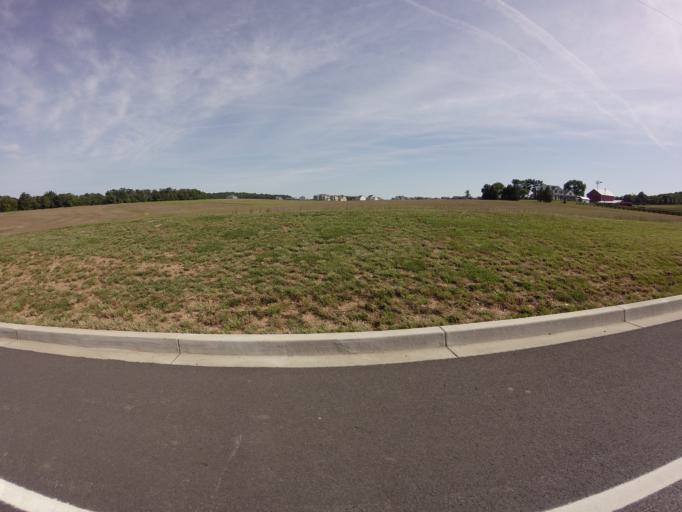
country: US
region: Maryland
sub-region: Frederick County
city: Green Valley
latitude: 39.3479
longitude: -77.2893
